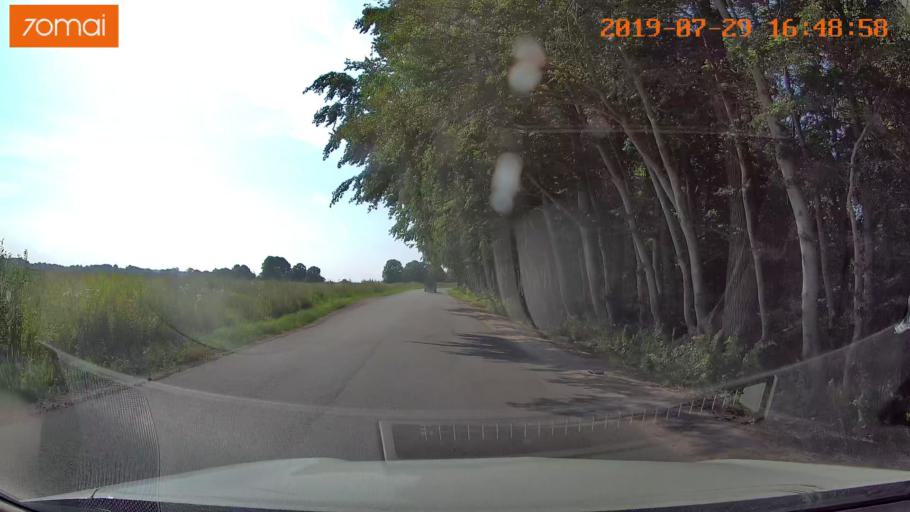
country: RU
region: Kaliningrad
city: Primorsk
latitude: 54.7908
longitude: 20.0707
